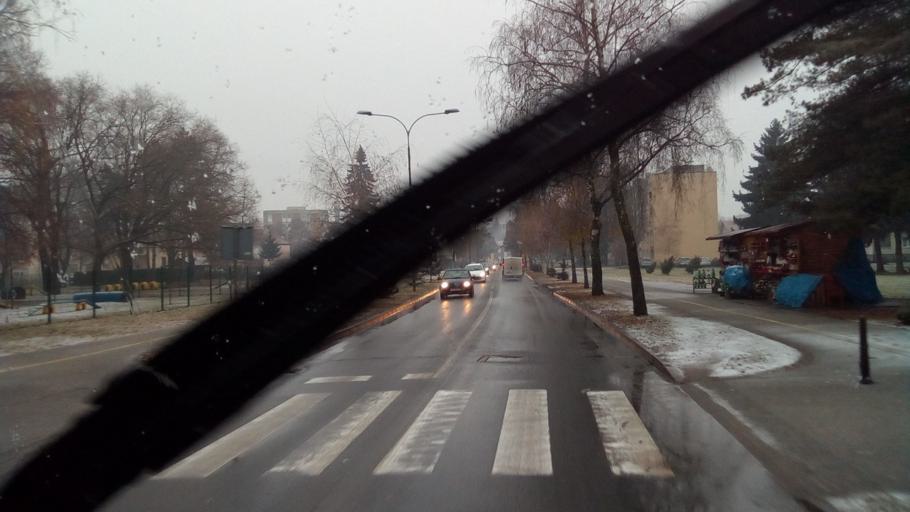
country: HR
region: Varazdinska
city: Varazdin
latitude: 46.3076
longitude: 16.3267
